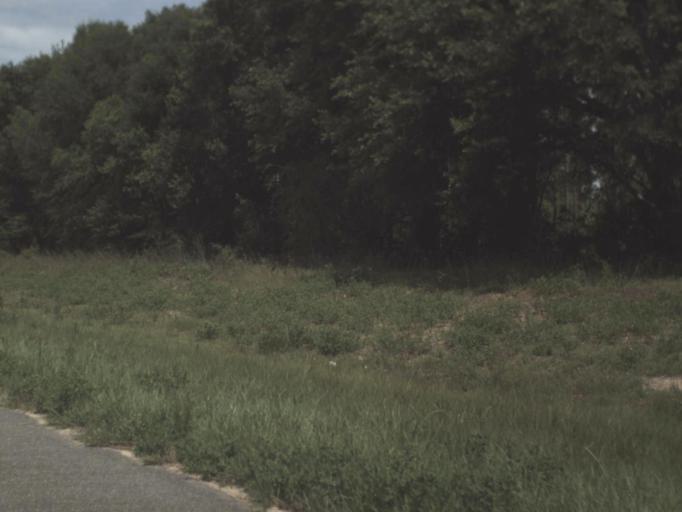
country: US
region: Florida
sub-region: Madison County
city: Madison
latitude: 30.4883
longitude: -83.4879
